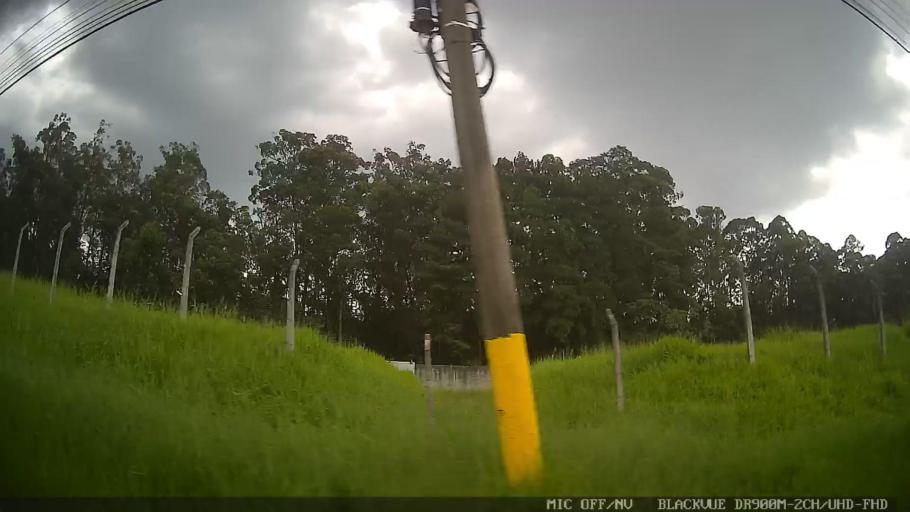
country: BR
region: Sao Paulo
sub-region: Suzano
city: Suzano
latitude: -23.5735
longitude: -46.3037
